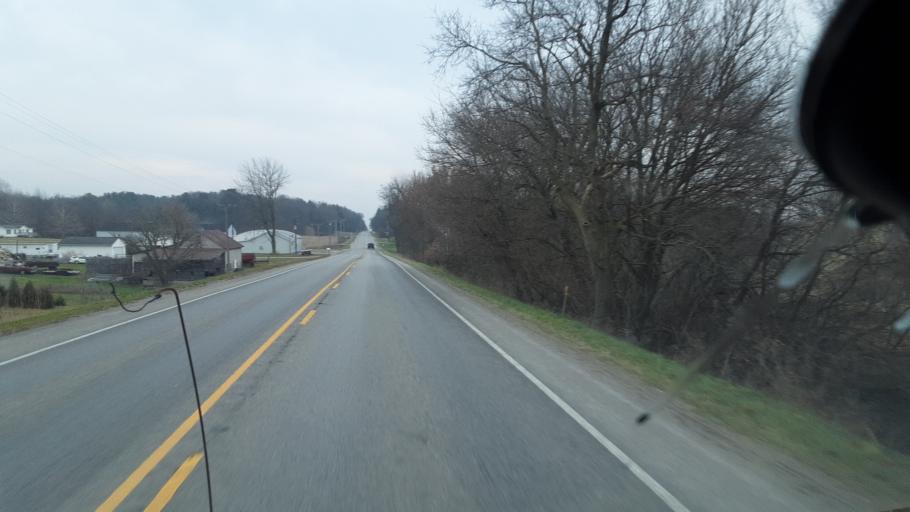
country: US
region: Indiana
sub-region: Elkhart County
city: Middlebury
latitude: 41.7260
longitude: -85.6542
